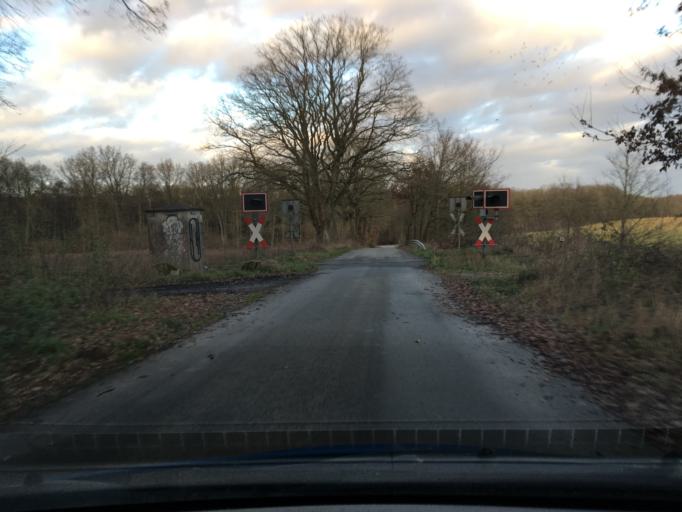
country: DE
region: Lower Saxony
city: Amelinghausen
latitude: 53.1384
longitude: 10.1885
